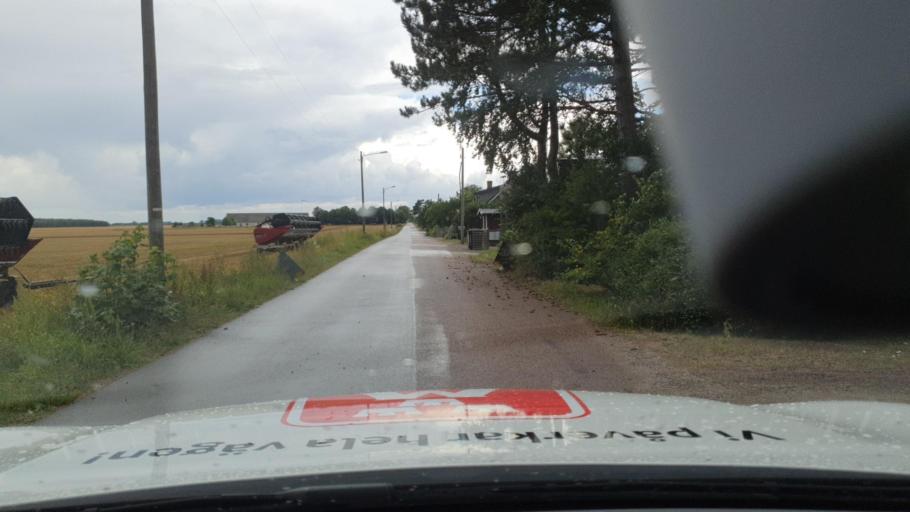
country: SE
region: Skane
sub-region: Angelholms Kommun
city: Strovelstorp
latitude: 56.1954
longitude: 12.7731
